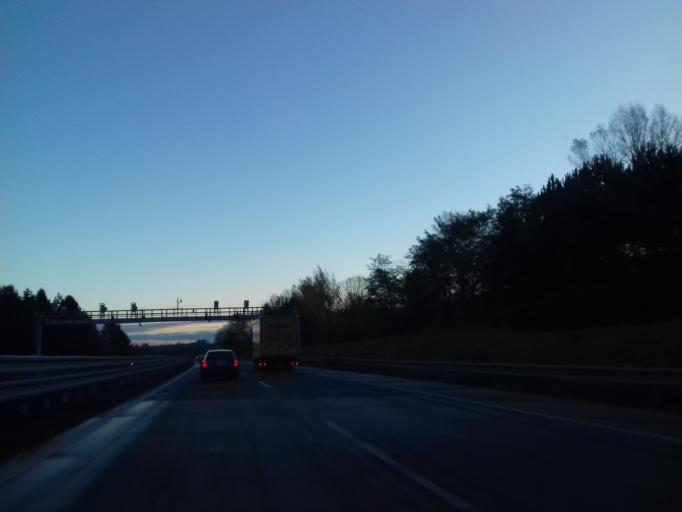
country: CZ
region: South Moravian
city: Rousinov
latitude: 49.2015
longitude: 16.9023
